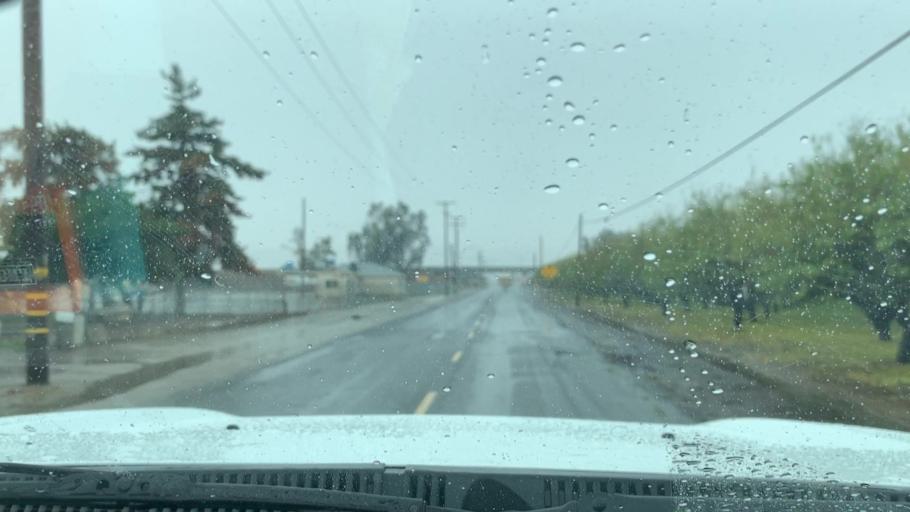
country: US
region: California
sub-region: Tulare County
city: Earlimart
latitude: 35.8337
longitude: -119.2571
